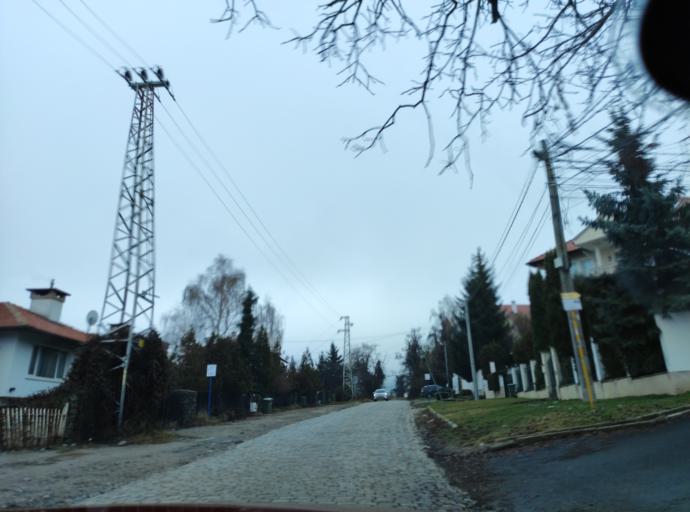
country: BG
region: Sofia-Capital
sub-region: Stolichna Obshtina
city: Sofia
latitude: 42.6253
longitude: 23.3081
